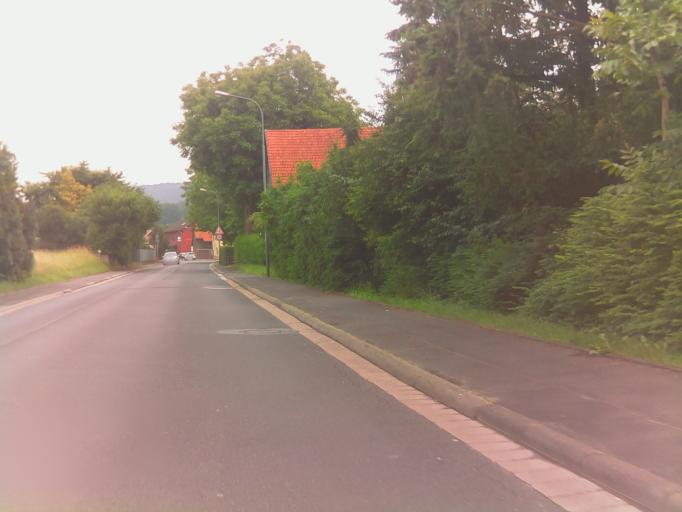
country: DE
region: Hesse
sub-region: Regierungsbezirk Darmstadt
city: Bad Soden-Salmunster
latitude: 50.2725
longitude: 9.3771
